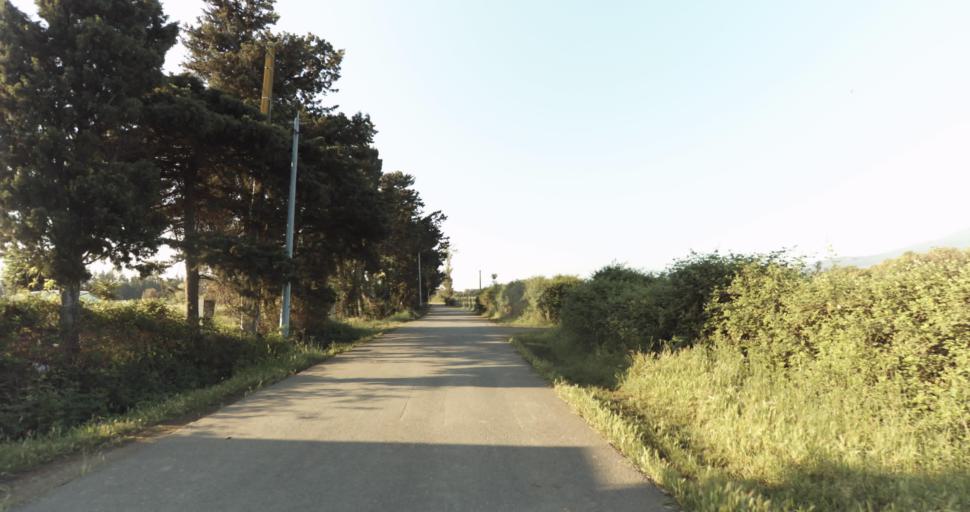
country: FR
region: Corsica
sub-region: Departement de la Haute-Corse
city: Biguglia
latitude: 42.6026
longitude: 9.4536
